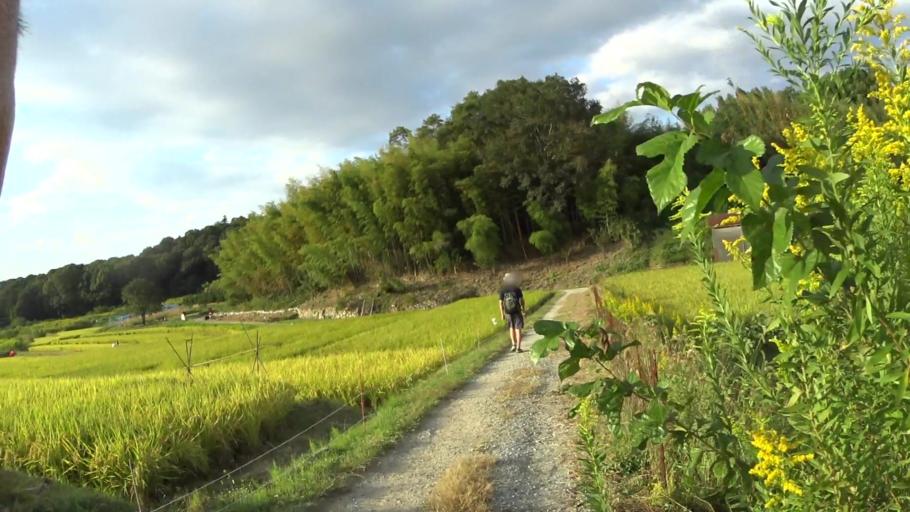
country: JP
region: Nara
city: Tenri
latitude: 34.5483
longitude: 135.8515
